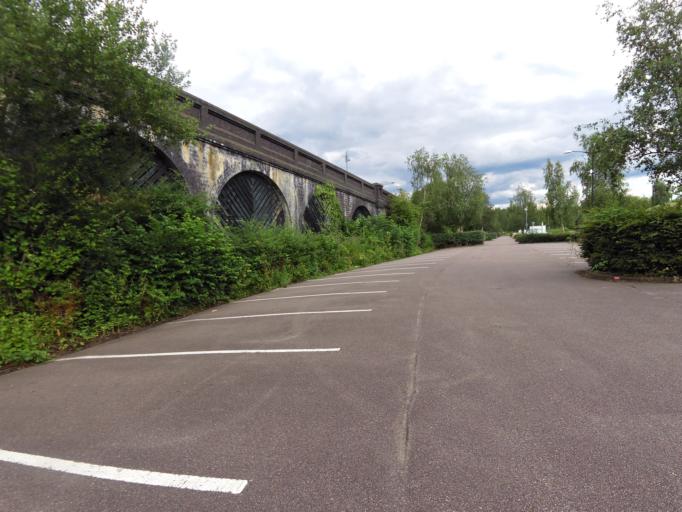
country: GB
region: England
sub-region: Hertfordshire
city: Broxbourne
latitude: 51.7447
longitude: -0.0113
